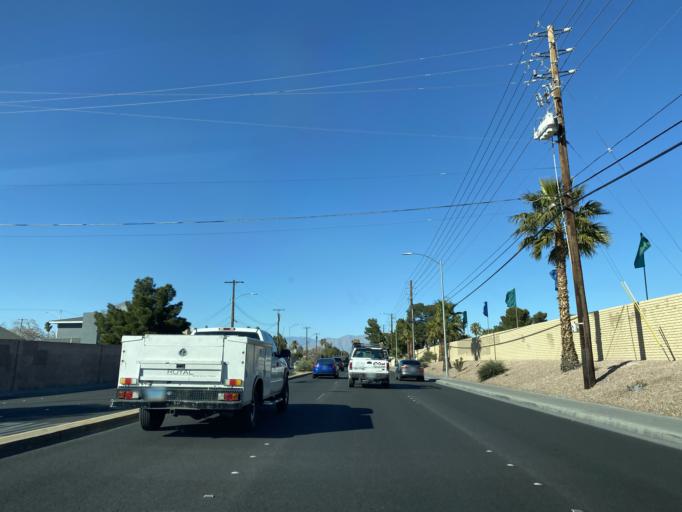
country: US
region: Nevada
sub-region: Clark County
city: Las Vegas
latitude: 36.1466
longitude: -115.1907
